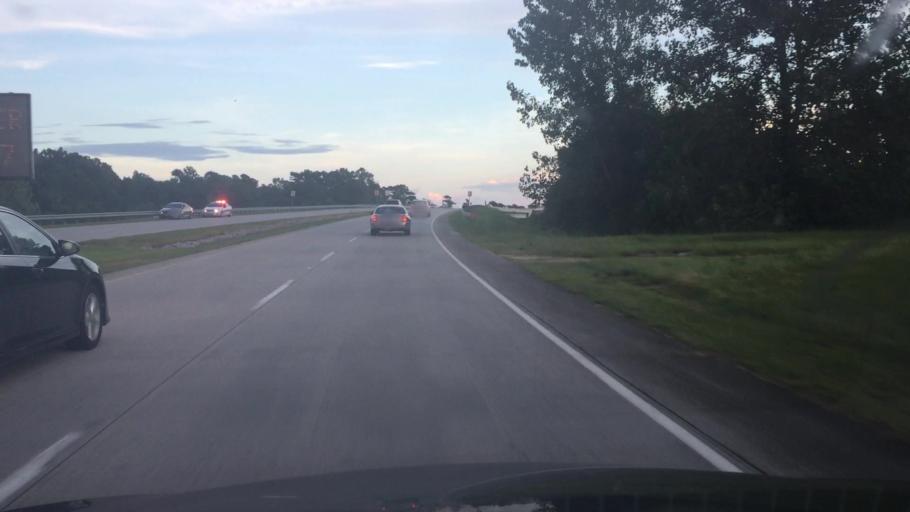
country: US
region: South Carolina
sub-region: Horry County
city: North Myrtle Beach
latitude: 33.8372
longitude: -78.6896
